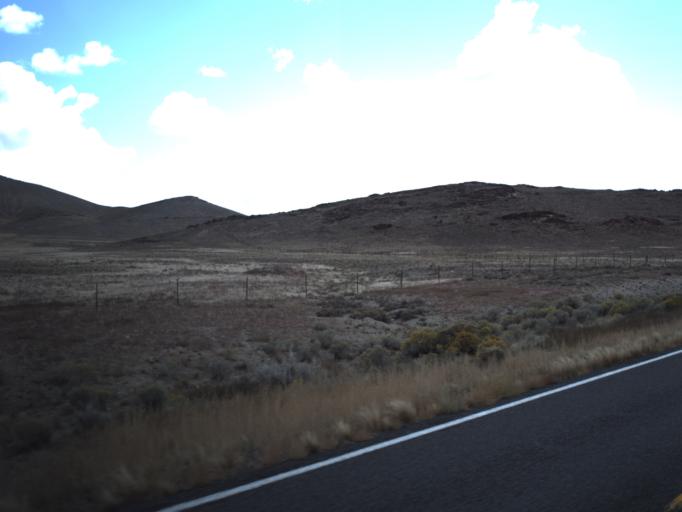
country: US
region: Utah
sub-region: Beaver County
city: Milford
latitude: 38.6325
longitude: -113.8553
